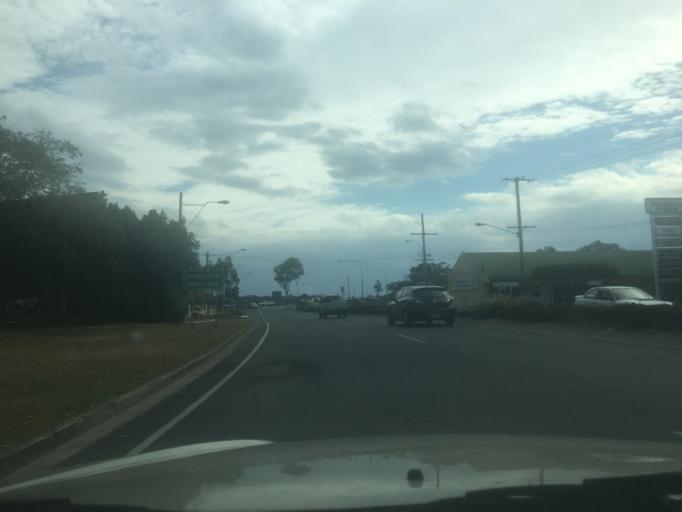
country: AU
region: Queensland
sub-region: Moreton Bay
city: Bongaree
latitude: -27.0669
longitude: 153.1494
